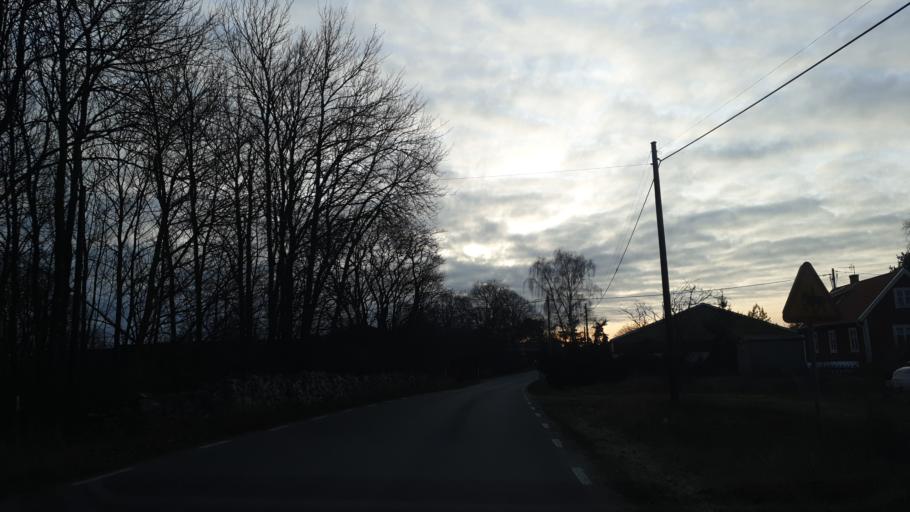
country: SE
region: Blekinge
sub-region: Karlskrona Kommun
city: Jaemjoe
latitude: 56.1905
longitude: 15.9475
